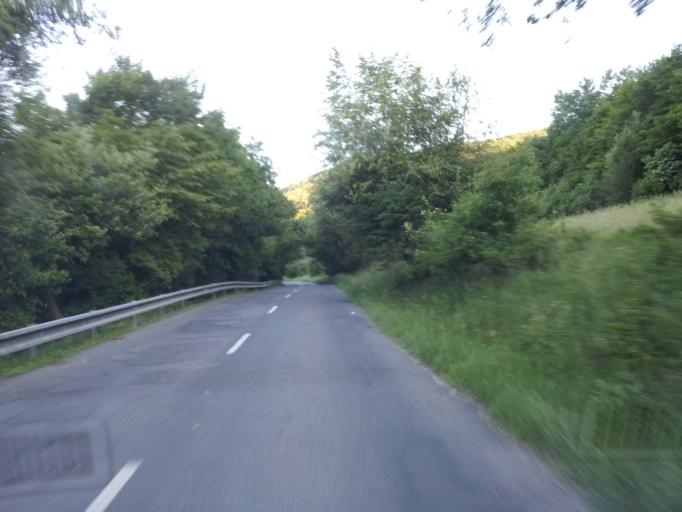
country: SK
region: Banskobystricky
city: Svaety Anton
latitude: 48.3356
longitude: 18.9541
